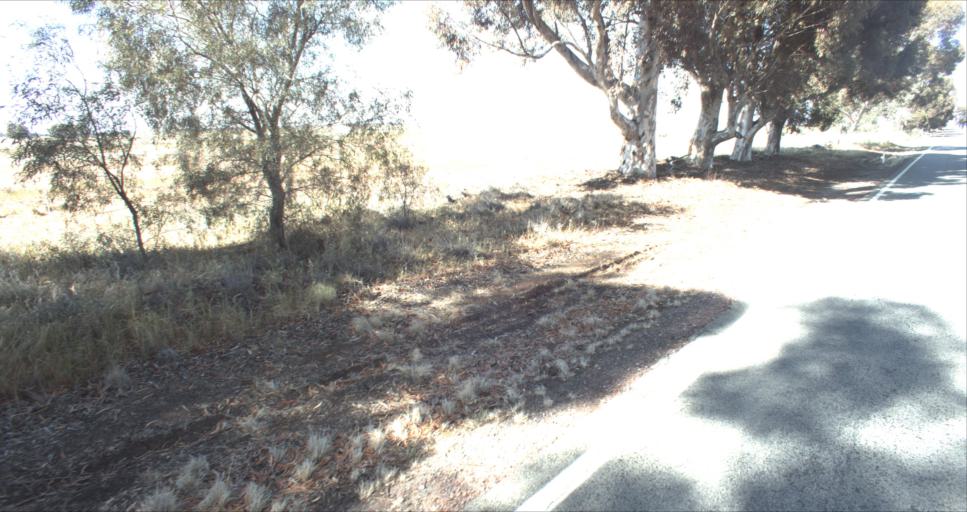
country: AU
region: New South Wales
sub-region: Leeton
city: Leeton
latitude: -34.5471
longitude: 146.3244
